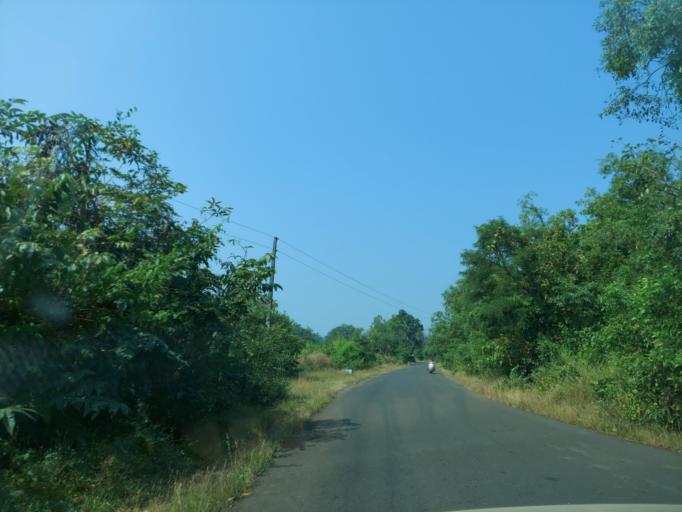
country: IN
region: Maharashtra
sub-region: Sindhudurg
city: Kudal
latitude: 15.9765
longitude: 73.6180
